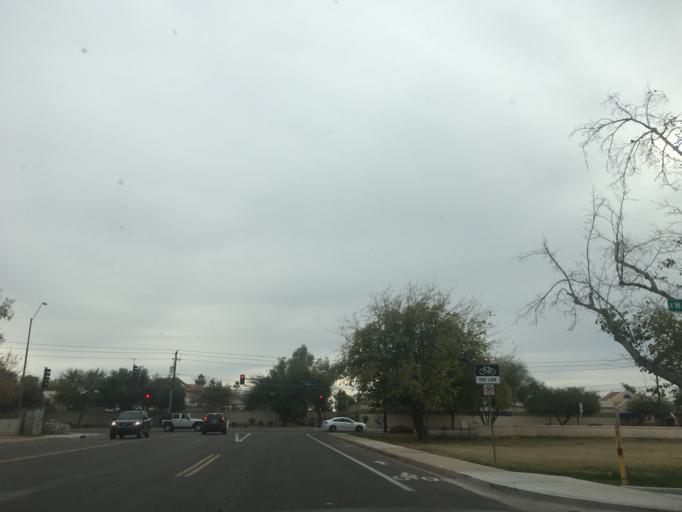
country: US
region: Arizona
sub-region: Maricopa County
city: Gilbert
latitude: 33.3507
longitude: -111.7818
